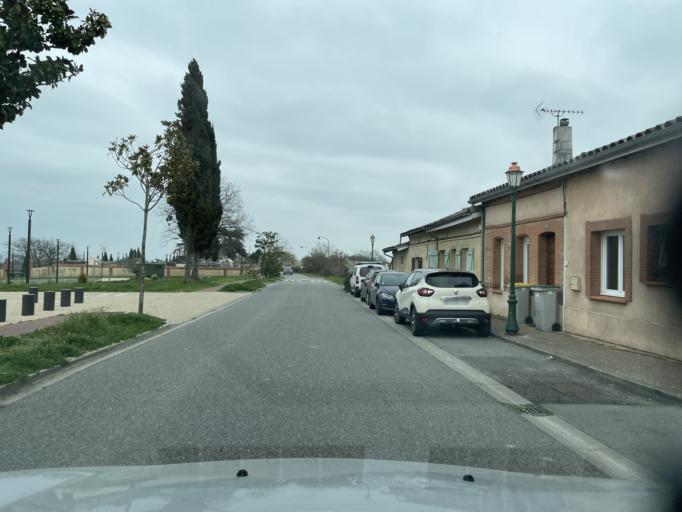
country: FR
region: Midi-Pyrenees
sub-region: Departement du Gers
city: Pujaudran
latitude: 43.5901
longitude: 1.1518
